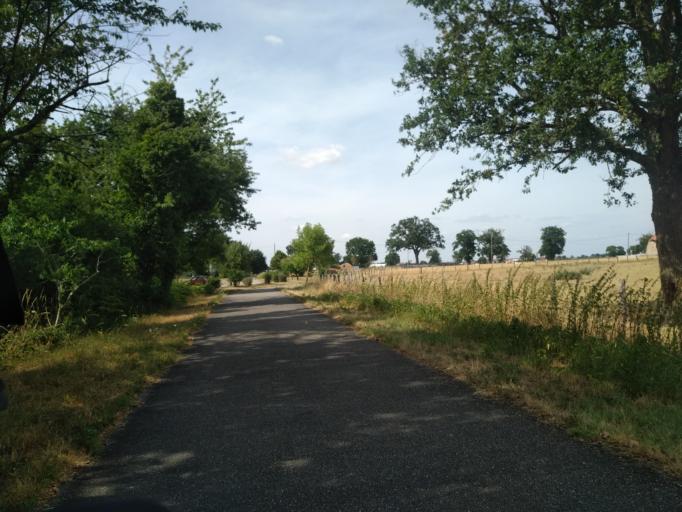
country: FR
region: Bourgogne
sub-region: Departement de Saone-et-Loire
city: Bourbon-Lancy
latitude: 46.6111
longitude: 3.7435
